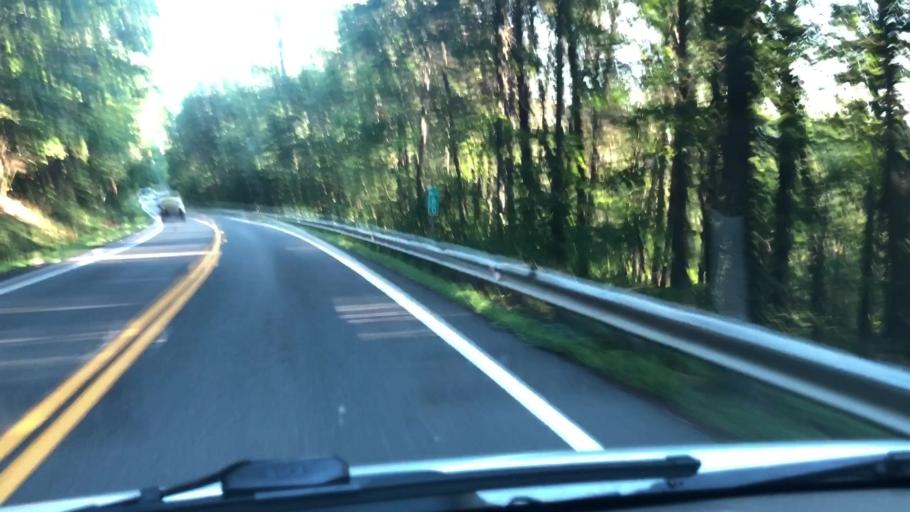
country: US
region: Massachusetts
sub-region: Hampshire County
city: Chesterfield
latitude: 42.3077
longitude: -72.8615
